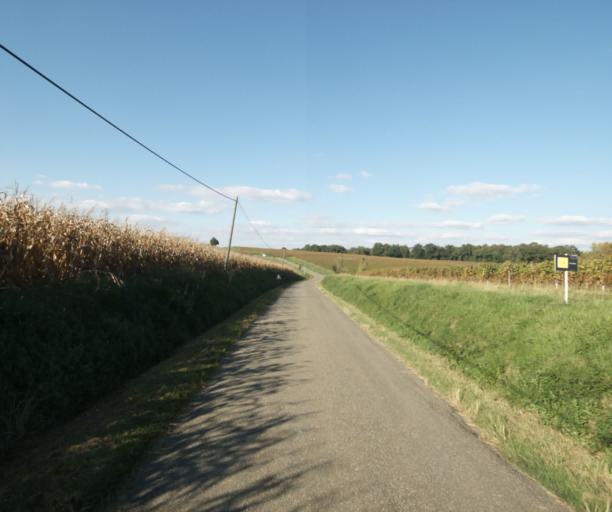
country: FR
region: Midi-Pyrenees
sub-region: Departement du Gers
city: Eauze
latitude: 43.7977
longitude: 0.1347
